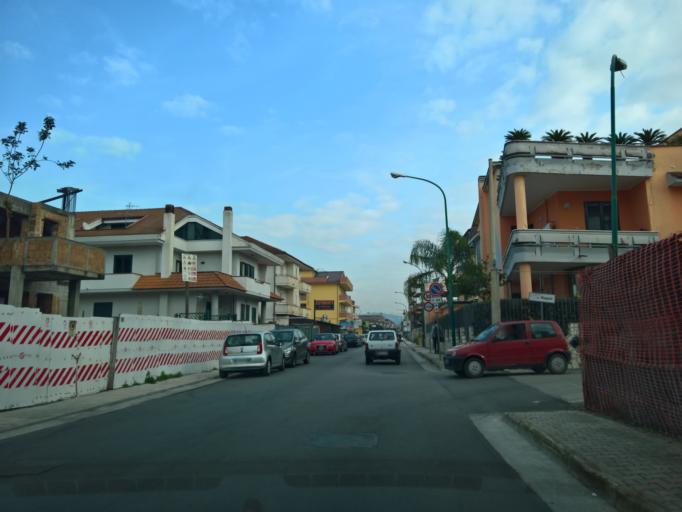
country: IT
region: Campania
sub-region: Provincia di Caserta
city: San Prisco
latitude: 41.0878
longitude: 14.2709
